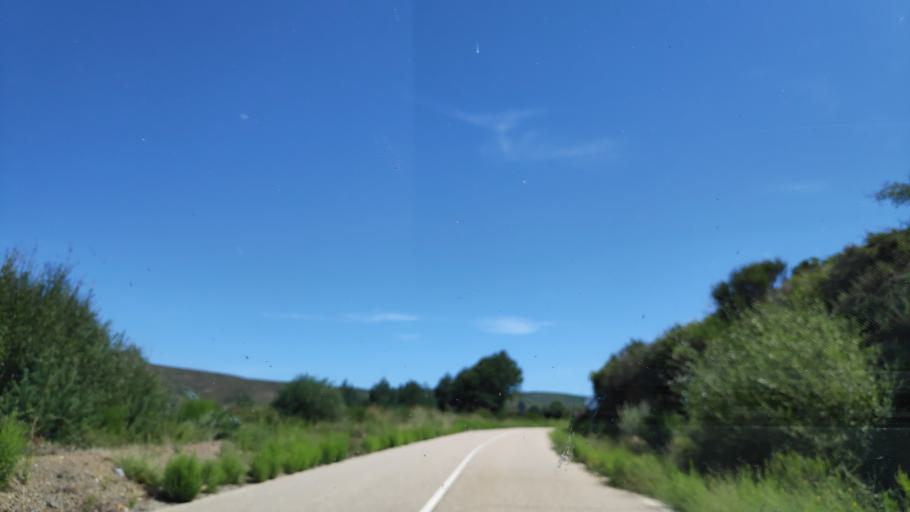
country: ES
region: Castille and Leon
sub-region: Provincia de Zamora
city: Requejo
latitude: 41.9908
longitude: -6.7044
